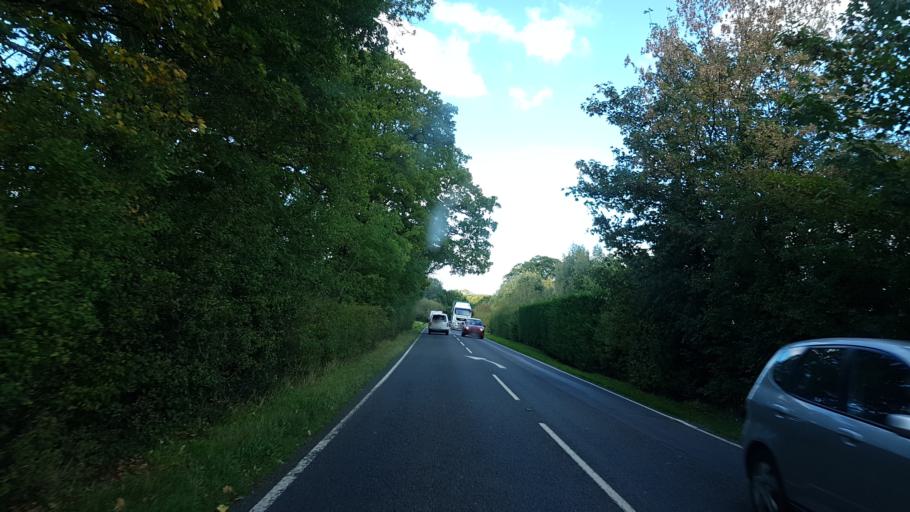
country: GB
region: England
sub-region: West Sussex
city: Petworth
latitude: 51.0459
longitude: -0.6422
